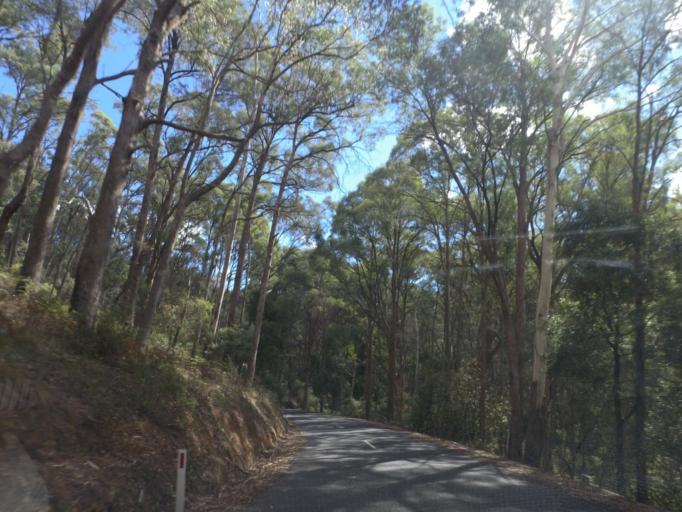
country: AU
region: Victoria
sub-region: Murrindindi
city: Alexandra
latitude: -37.3407
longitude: 145.9640
